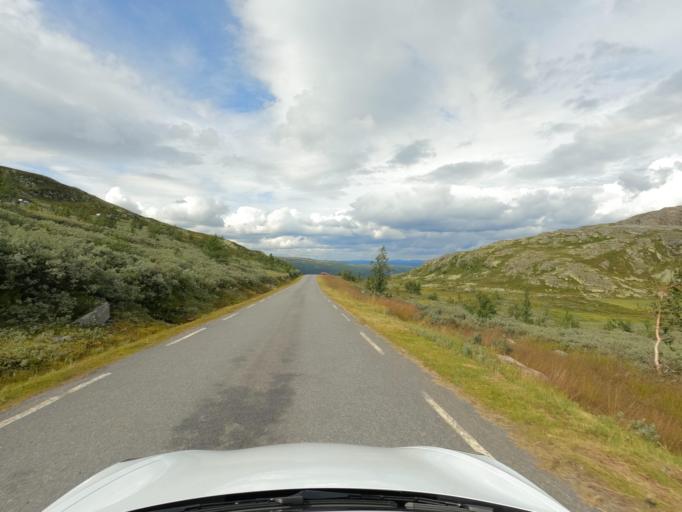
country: NO
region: Telemark
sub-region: Tinn
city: Rjukan
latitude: 59.8516
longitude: 8.6904
